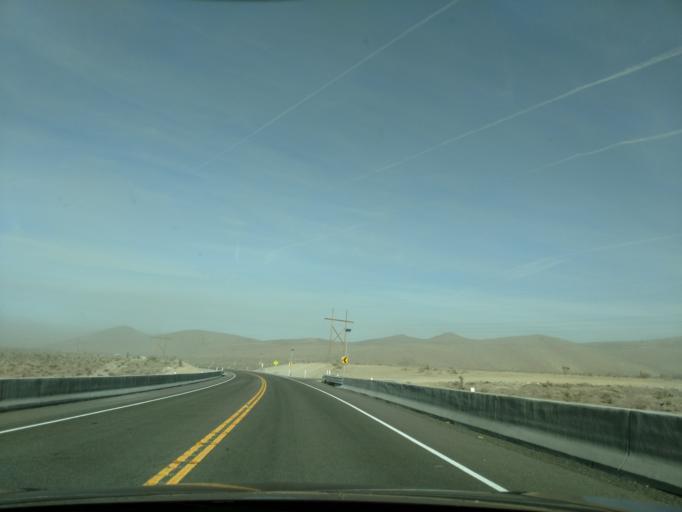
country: US
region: Nevada
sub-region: Nye County
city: Pahrump
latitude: 36.4337
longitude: -116.0730
